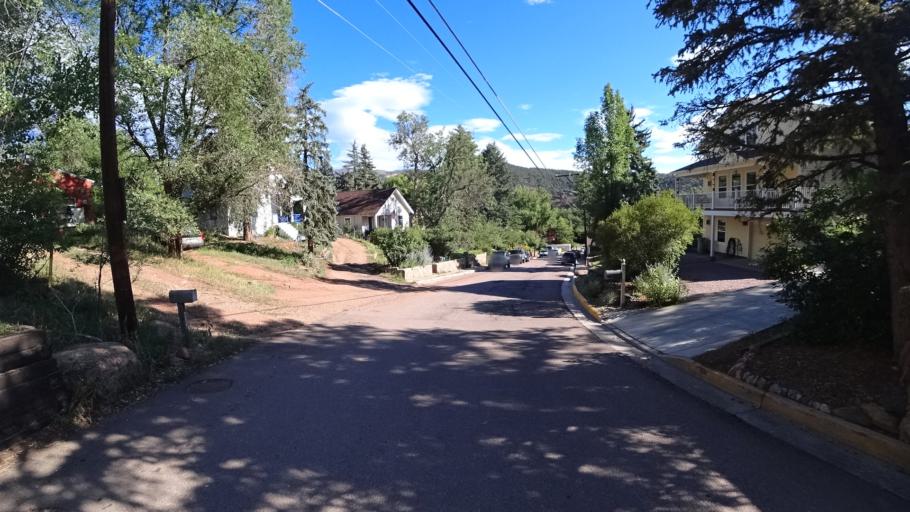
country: US
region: Colorado
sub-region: El Paso County
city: Manitou Springs
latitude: 38.8553
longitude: -104.9130
